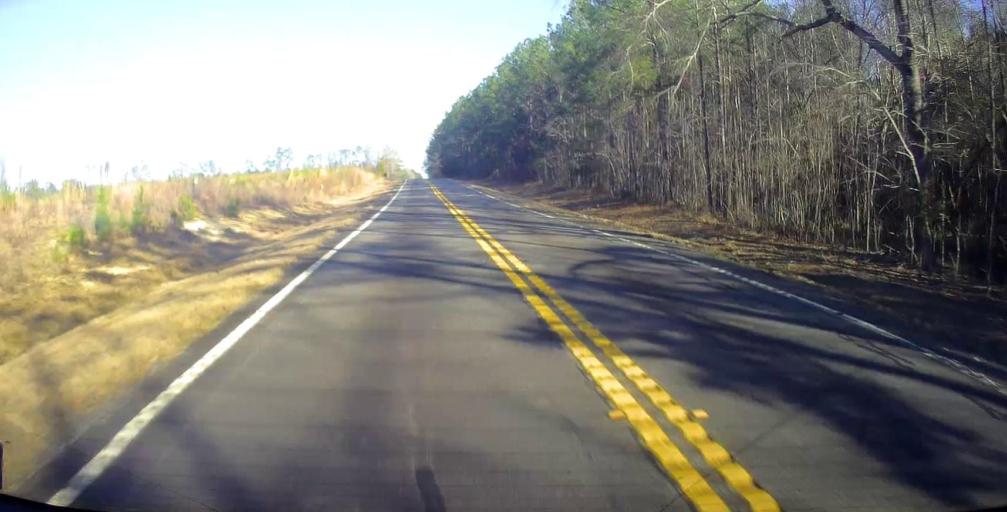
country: US
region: Georgia
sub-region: Talbot County
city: Talbotton
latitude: 32.6723
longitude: -84.4886
